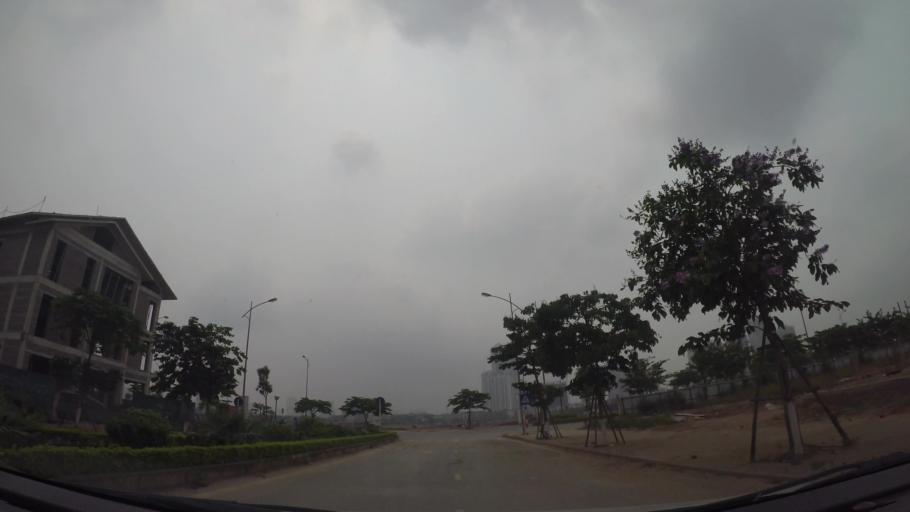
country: VN
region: Ha Noi
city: Ha Dong
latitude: 20.9823
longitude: 105.7552
